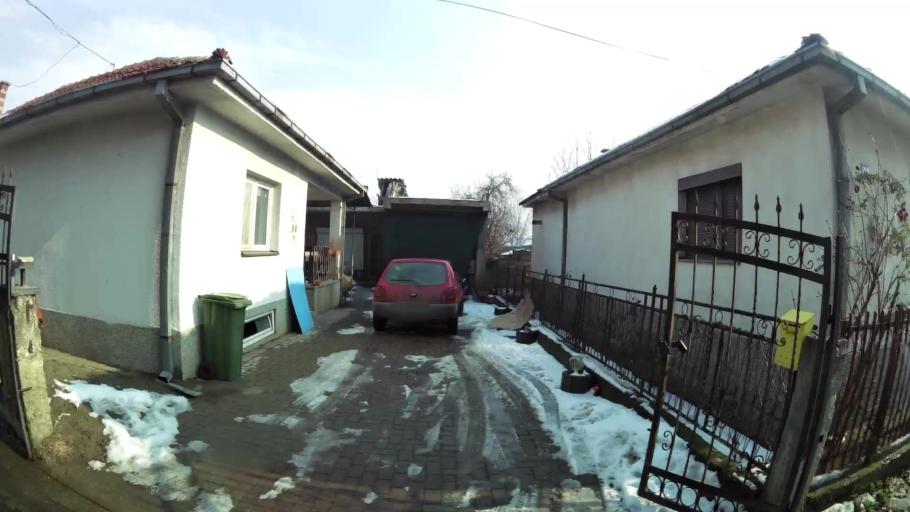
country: MK
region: Kisela Voda
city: Kisela Voda
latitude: 41.9924
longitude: 21.5013
